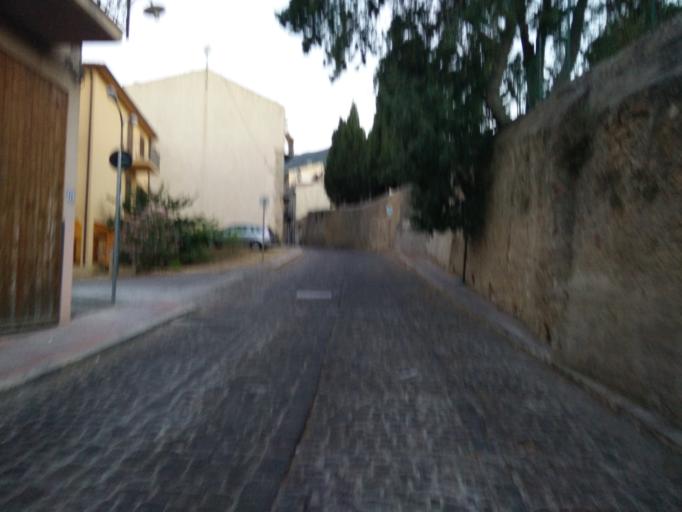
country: IT
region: Sicily
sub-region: Palermo
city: Castelbuono
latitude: 37.9270
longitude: 14.0875
